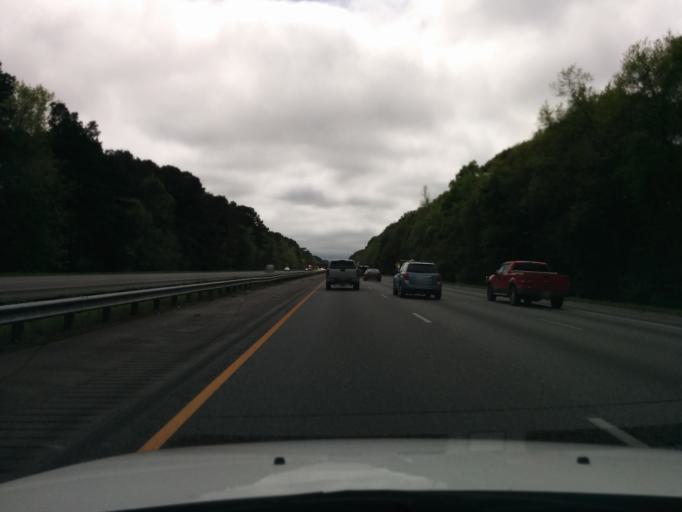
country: US
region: Georgia
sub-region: Chatham County
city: Georgetown
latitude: 32.0344
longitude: -81.2662
